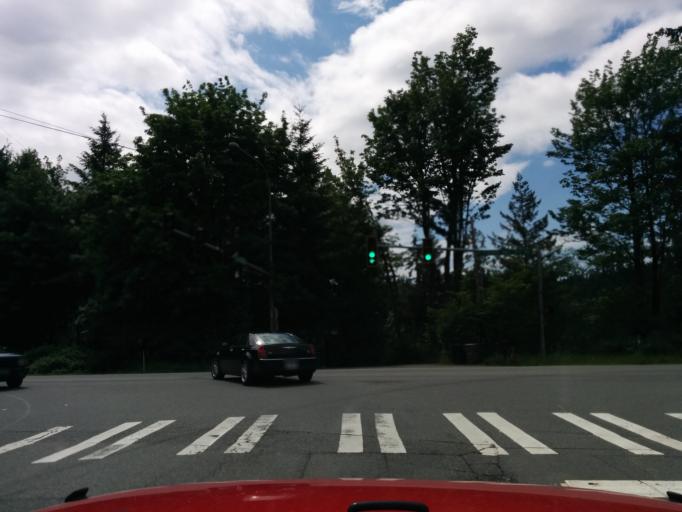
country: US
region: Washington
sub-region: King County
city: Union Hill-Novelty Hill
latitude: 47.6444
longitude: -122.0247
